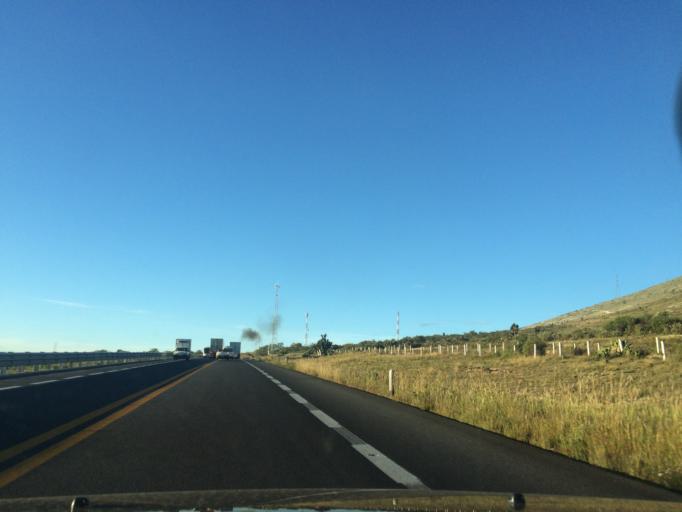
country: MX
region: Puebla
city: Morelos Canada
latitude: 18.7198
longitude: -97.4722
